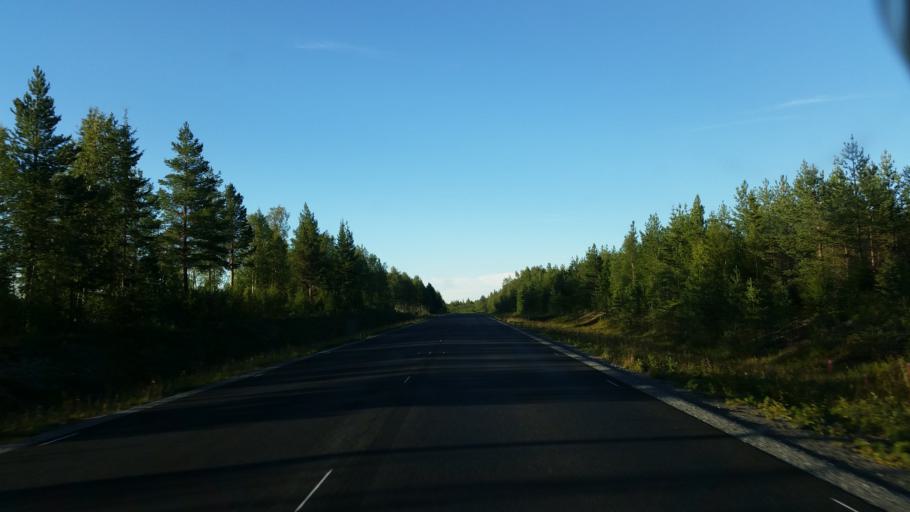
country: SE
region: Vaesterbotten
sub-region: Dorotea Kommun
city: Dorotea
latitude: 64.3306
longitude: 16.6329
